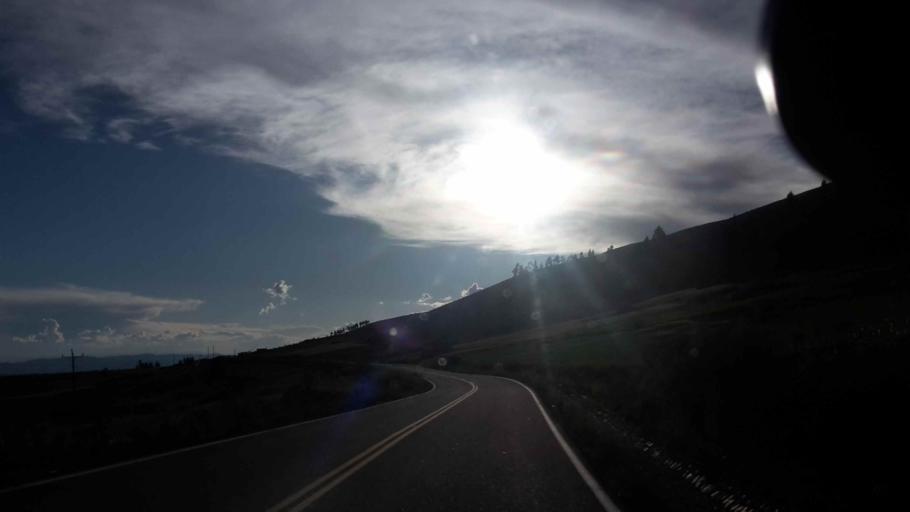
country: BO
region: Cochabamba
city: Arani
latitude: -17.5584
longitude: -65.7012
